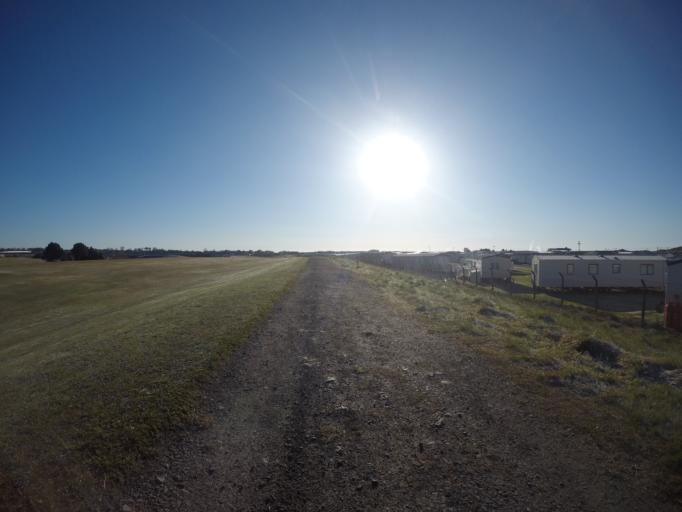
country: GB
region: Scotland
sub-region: North Ayrshire
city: Stevenston
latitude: 55.6341
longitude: -4.7665
